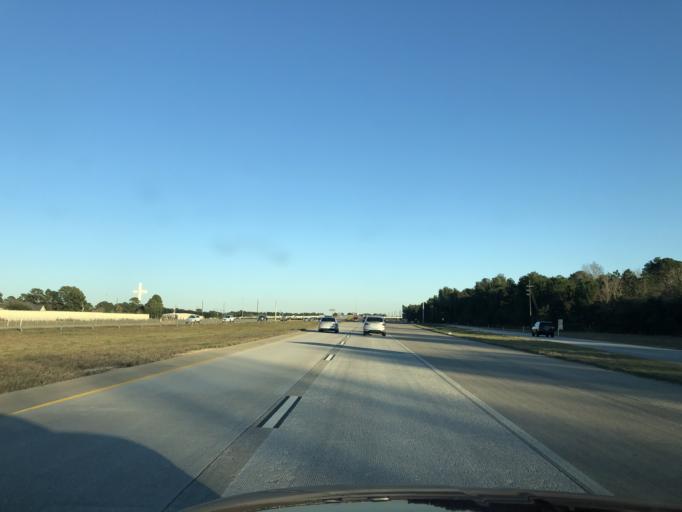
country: US
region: Texas
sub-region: Harris County
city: Tomball
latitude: 30.0520
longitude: -95.6286
